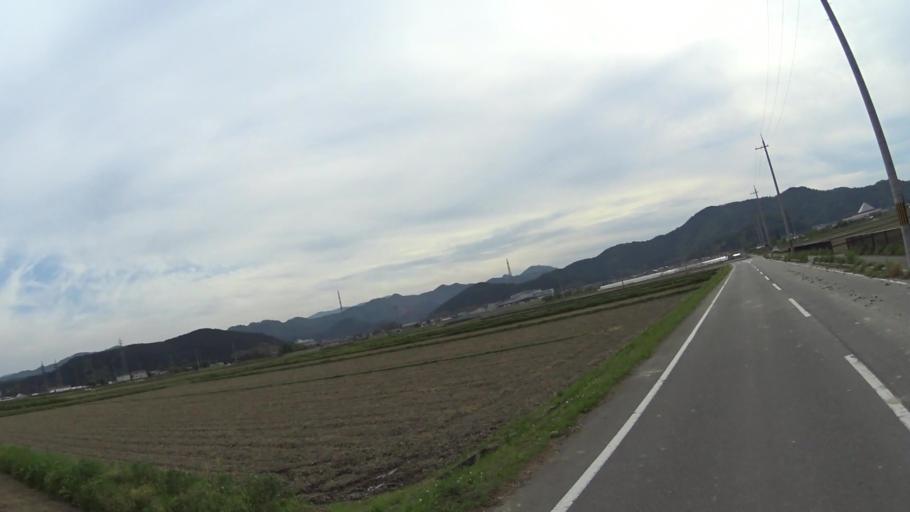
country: JP
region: Kyoto
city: Kameoka
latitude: 35.0892
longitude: 135.5506
